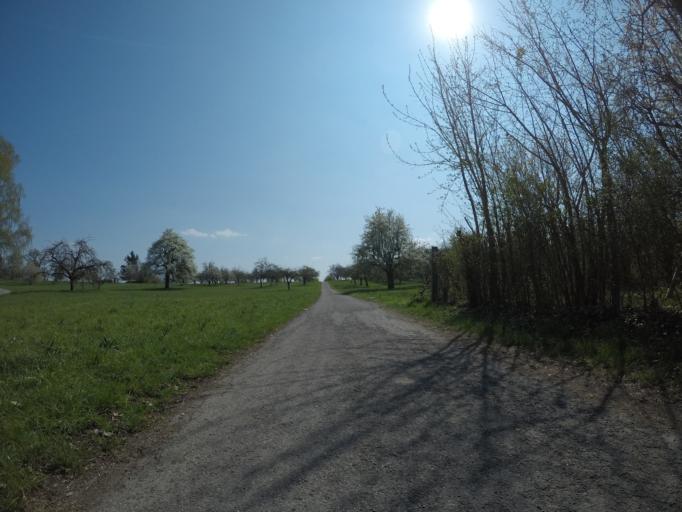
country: DE
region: Baden-Wuerttemberg
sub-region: Tuebingen Region
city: Reutlingen
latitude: 48.4887
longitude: 9.1789
